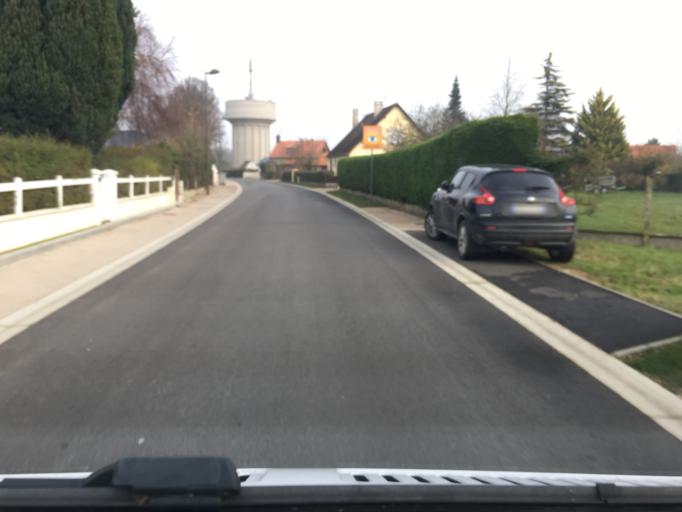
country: FR
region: Picardie
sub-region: Departement de la Somme
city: Saint-Valery-sur-Somme
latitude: 50.1790
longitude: 1.6311
